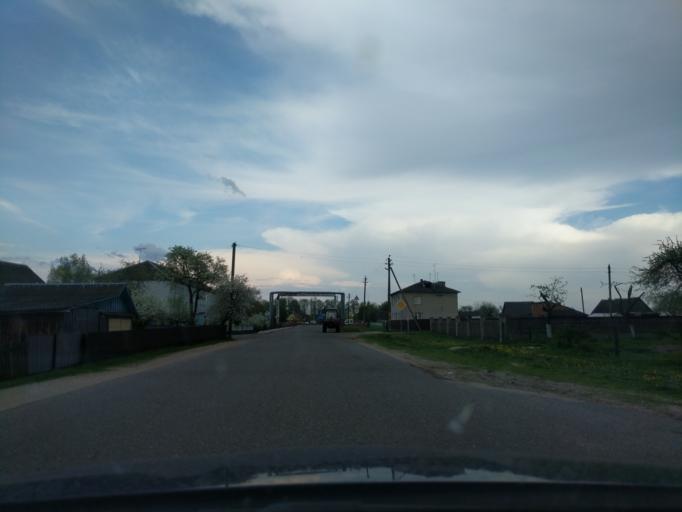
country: BY
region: Grodnenskaya
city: Lyubcha
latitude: 53.7509
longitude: 26.0618
